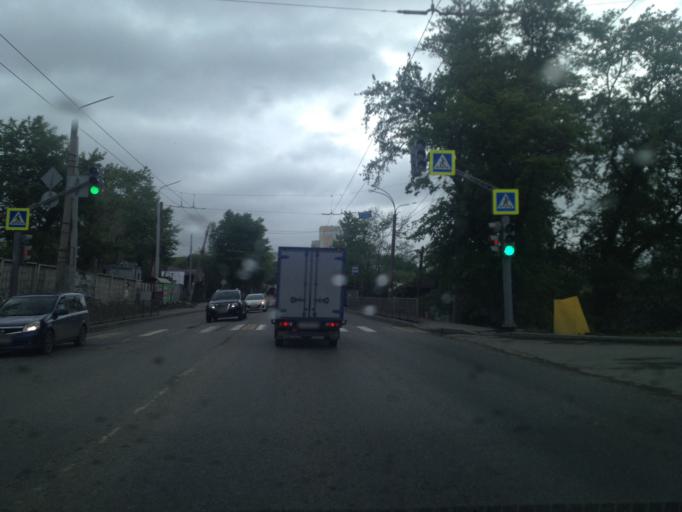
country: RU
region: Sverdlovsk
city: Yekaterinburg
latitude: 56.7780
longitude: 60.6606
